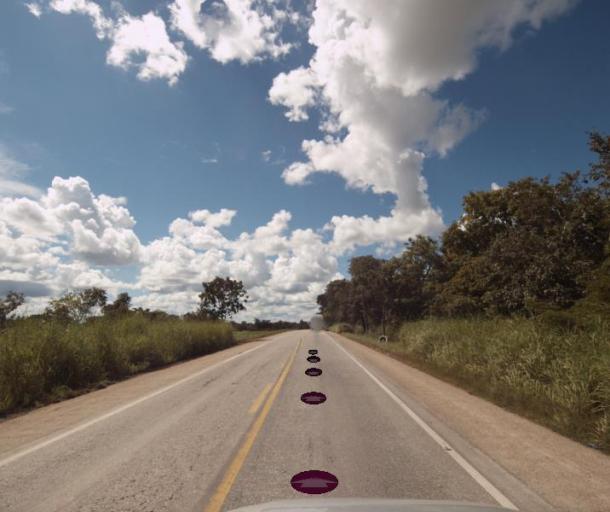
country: BR
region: Goias
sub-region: Porangatu
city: Porangatu
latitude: -13.6008
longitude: -49.0420
